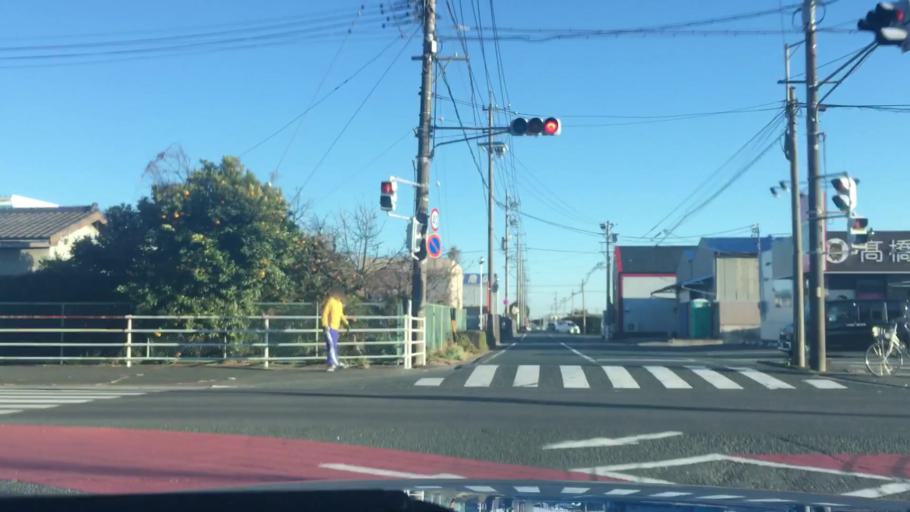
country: JP
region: Shizuoka
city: Hamamatsu
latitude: 34.7648
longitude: 137.6853
